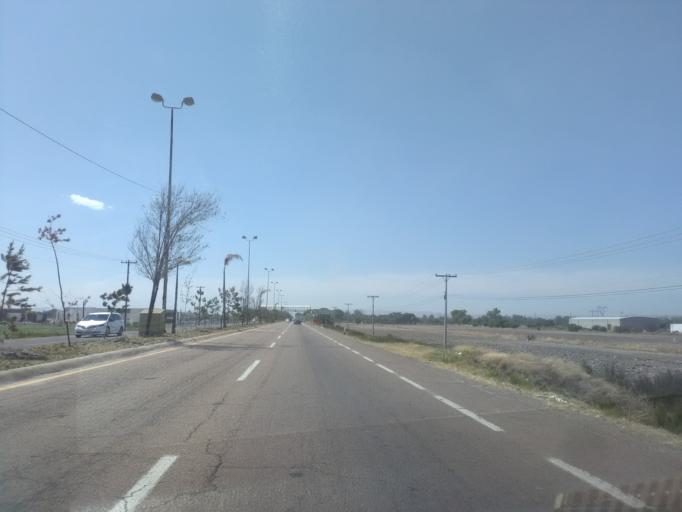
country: MX
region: Durango
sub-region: Durango
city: Jose Refugio Salcido
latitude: 24.0237
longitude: -104.5491
